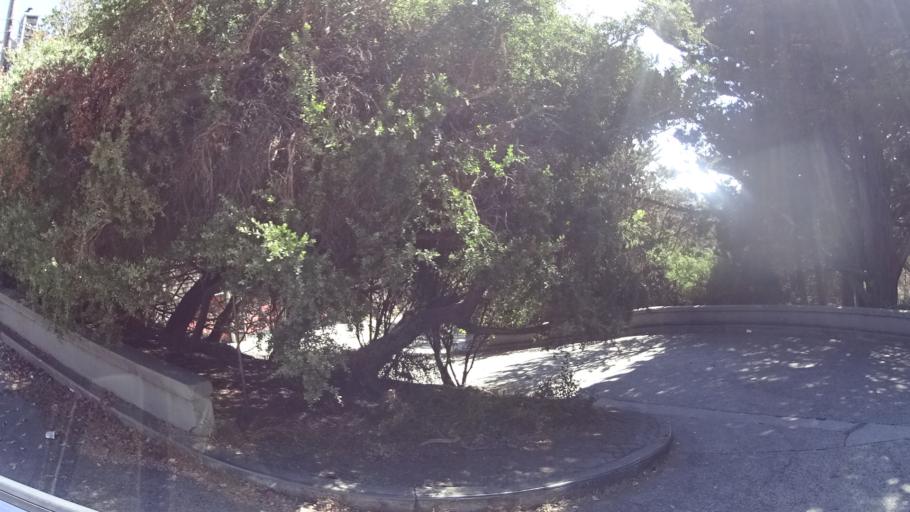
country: US
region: California
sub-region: San Francisco County
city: San Francisco
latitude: 37.7589
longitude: -122.4040
